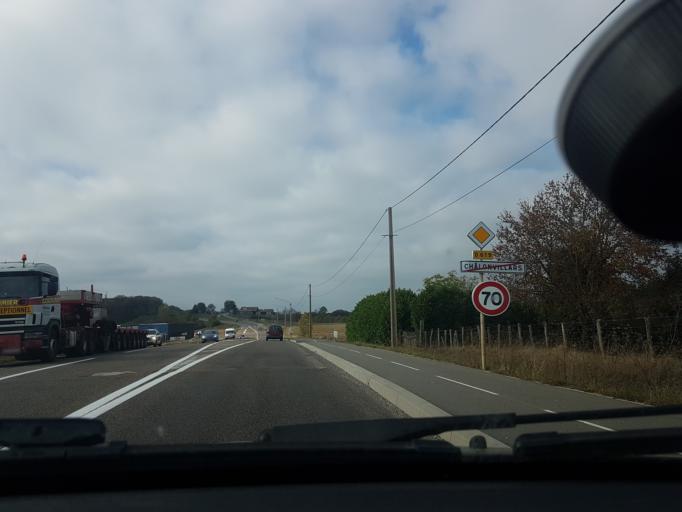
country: FR
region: Franche-Comte
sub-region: Departement de la Haute-Saone
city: Chalonvillars
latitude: 47.6453
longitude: 6.7819
